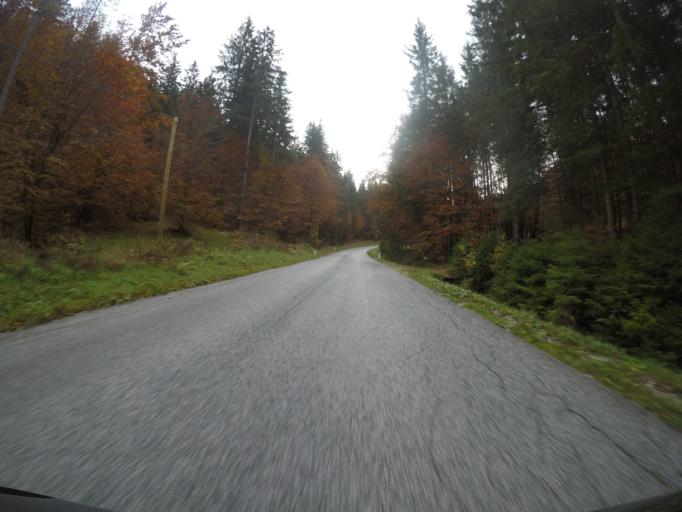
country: SI
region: Kranjska Gora
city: Mojstrana
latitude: 46.4449
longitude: 13.9325
